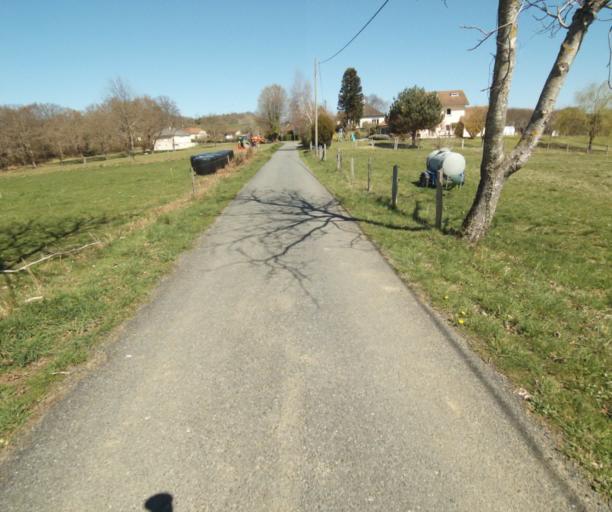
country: FR
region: Limousin
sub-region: Departement de la Correze
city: Saint-Clement
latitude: 45.3375
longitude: 1.6945
